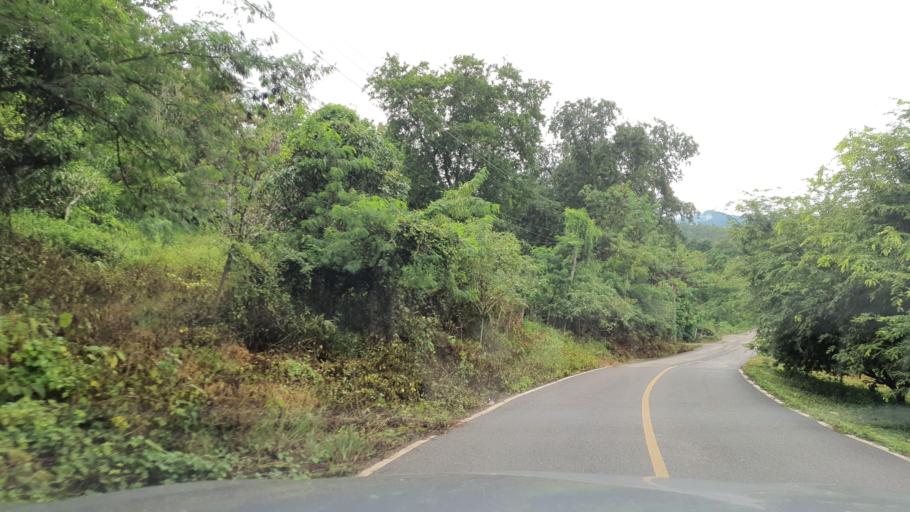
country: TH
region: Chiang Mai
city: Mae Taeng
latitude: 19.1958
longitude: 98.9414
